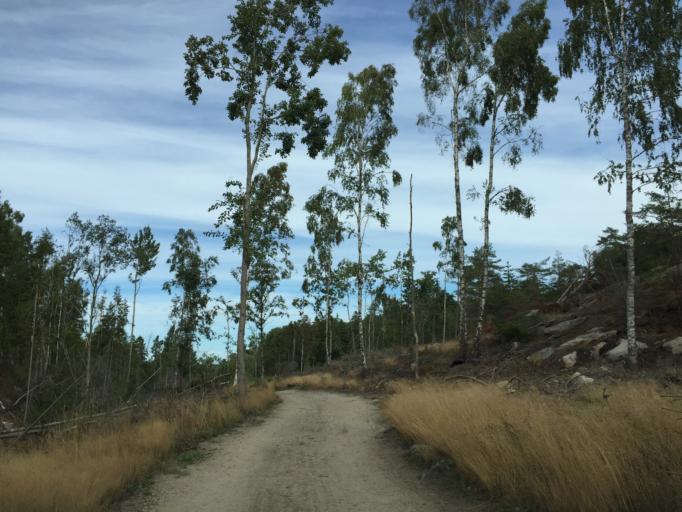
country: NO
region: Ostfold
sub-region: Fredrikstad
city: Fredrikstad
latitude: 59.0962
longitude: 10.9264
